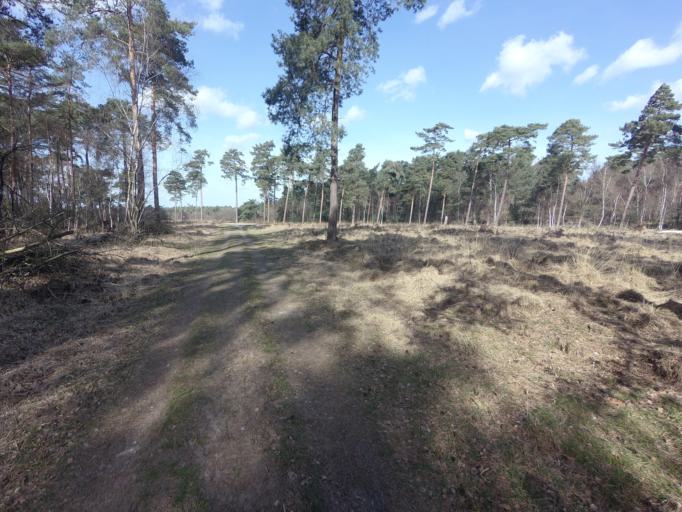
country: DE
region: North Rhine-Westphalia
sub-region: Regierungsbezirk Koln
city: Wassenberg
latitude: 51.1548
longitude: 6.1377
